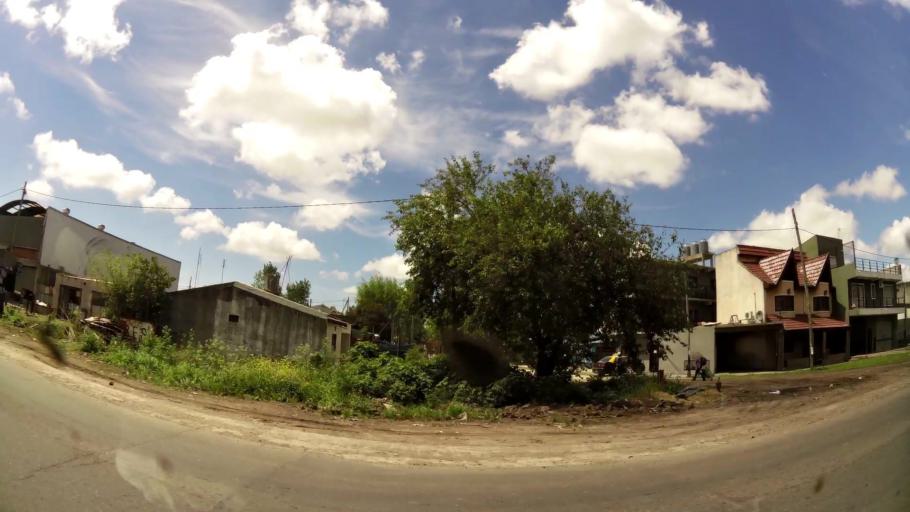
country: AR
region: Buenos Aires
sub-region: Partido de Quilmes
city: Quilmes
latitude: -34.8122
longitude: -58.2299
